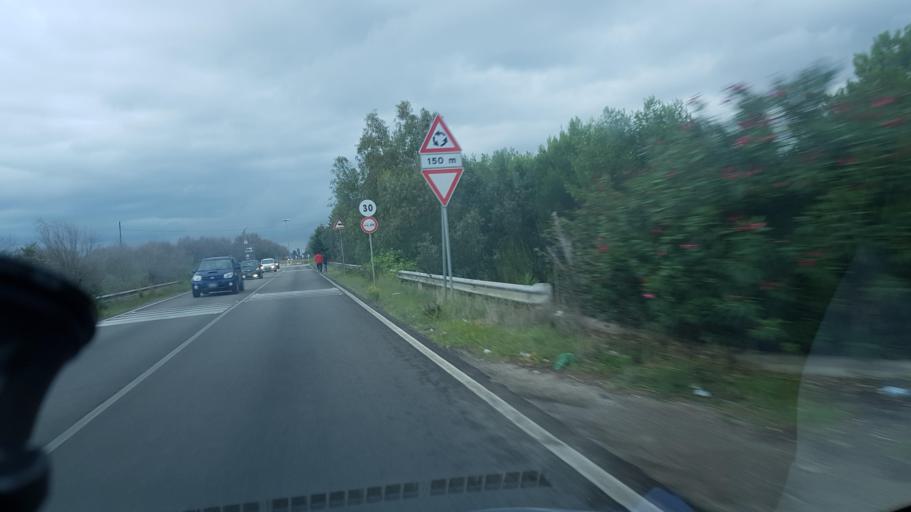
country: IT
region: Apulia
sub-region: Provincia di Lecce
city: Arnesano
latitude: 40.3615
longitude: 18.0957
